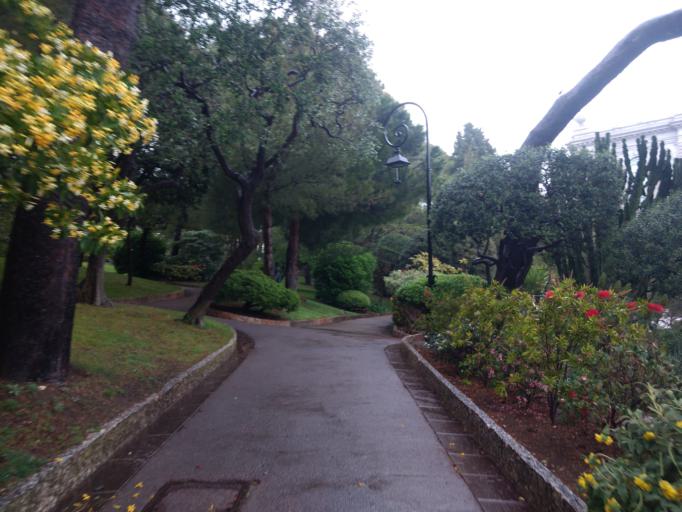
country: MC
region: Commune de Monaco
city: La Condamine
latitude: 43.7297
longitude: 7.4242
